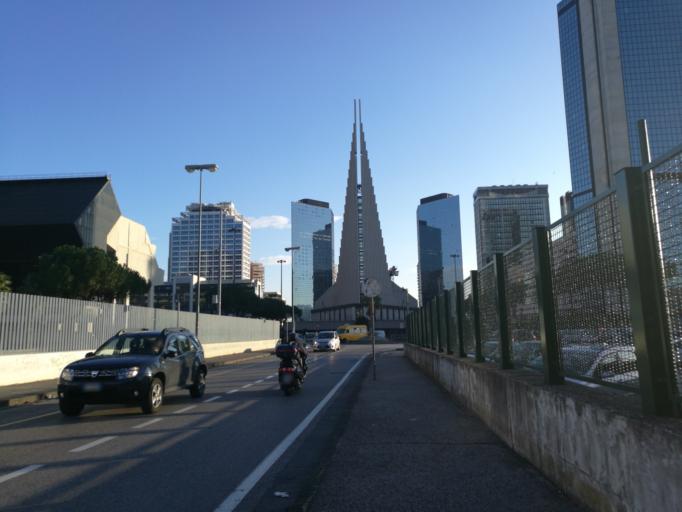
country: IT
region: Campania
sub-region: Provincia di Napoli
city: Napoli
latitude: 40.8605
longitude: 14.2814
